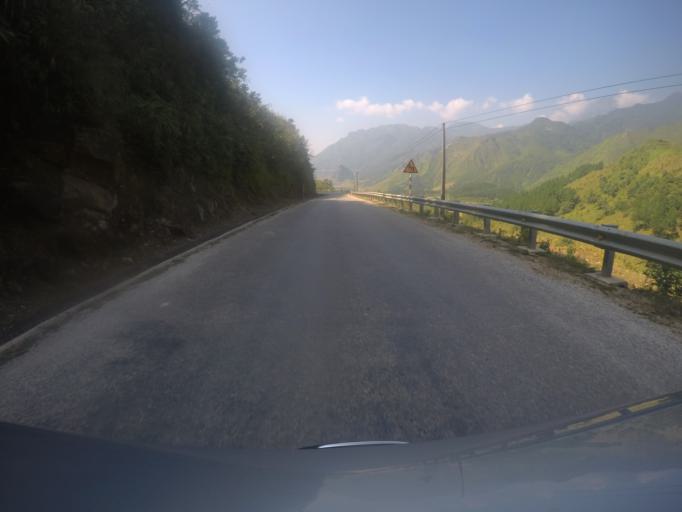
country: VN
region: Lai Chau
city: Than Uyen
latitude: 22.0368
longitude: 103.9467
